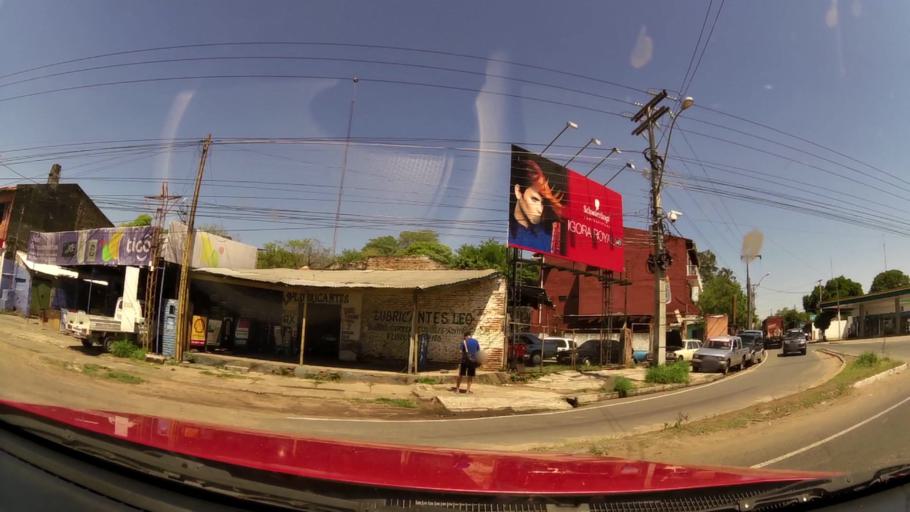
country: PY
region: Central
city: Colonia Mariano Roque Alonso
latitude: -25.2500
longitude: -57.5531
